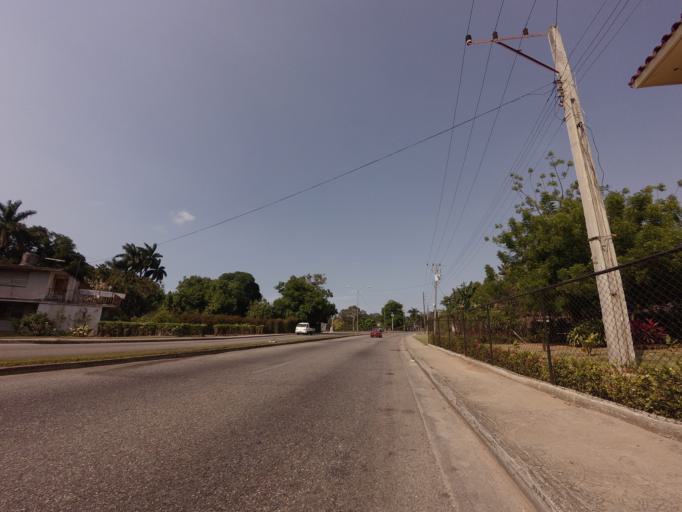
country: CU
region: La Habana
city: Cerro
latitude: 23.0790
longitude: -82.4487
